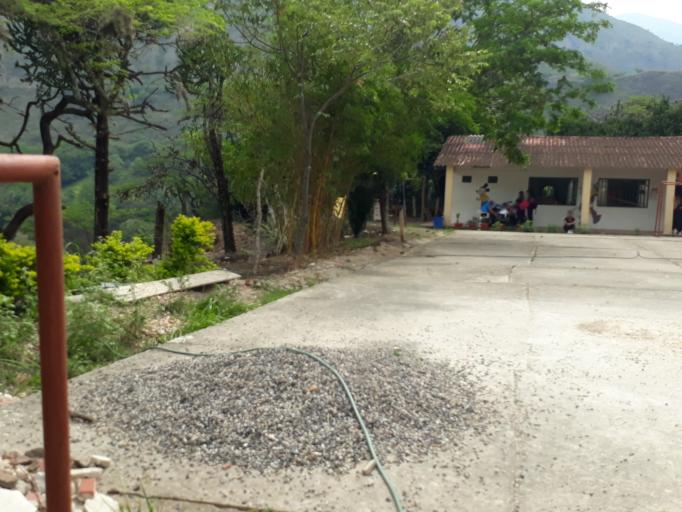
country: CO
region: Boyaca
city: Soata
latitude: 6.3243
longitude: -72.6501
